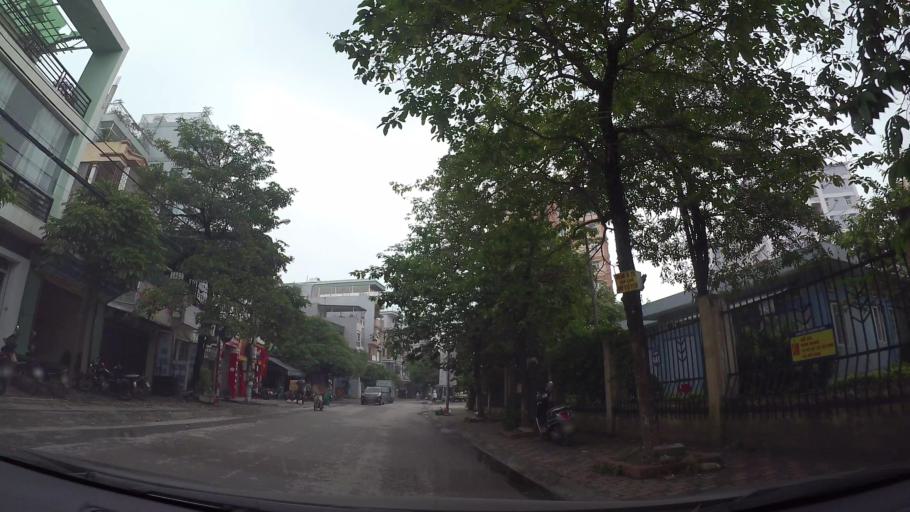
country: VN
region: Ha Noi
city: Van Dien
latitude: 20.9717
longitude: 105.8492
